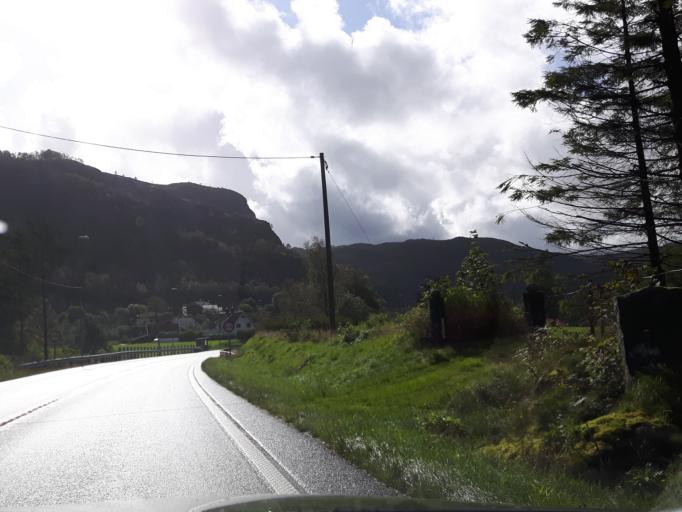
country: NO
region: Rogaland
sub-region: Sokndal
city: Hauge i Dalane
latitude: 58.4762
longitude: 6.3592
